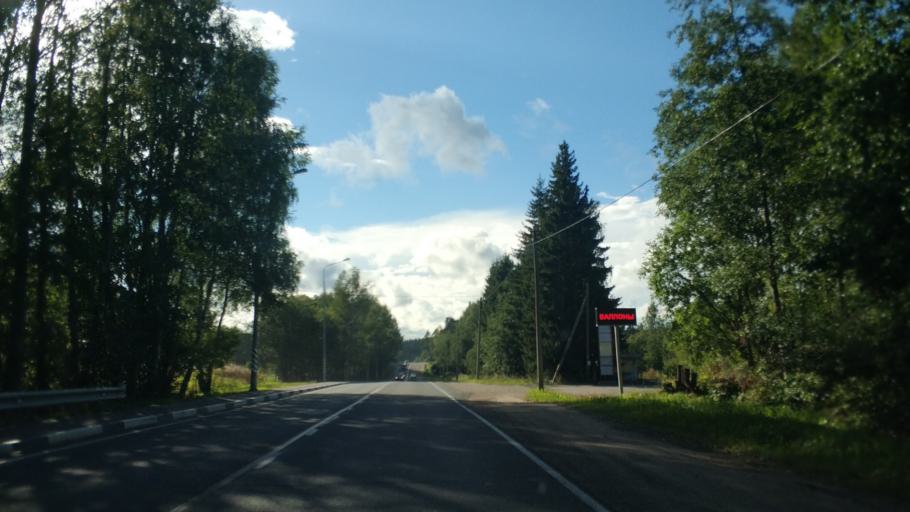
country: RU
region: Republic of Karelia
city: Lakhdenpokh'ya
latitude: 61.5231
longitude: 30.1731
